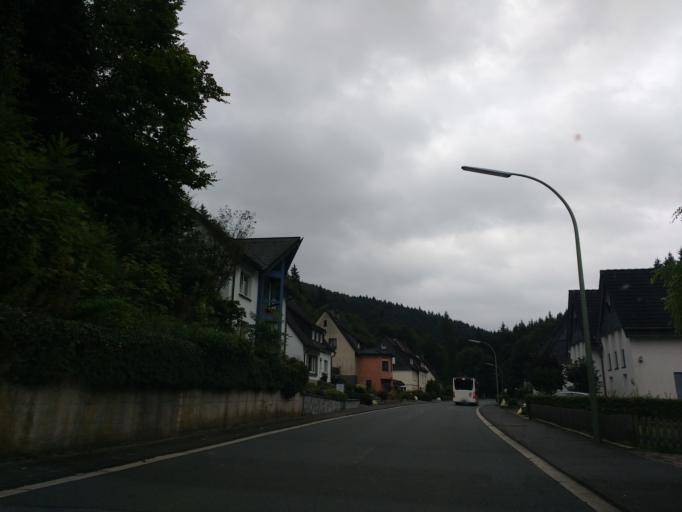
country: DE
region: North Rhine-Westphalia
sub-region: Regierungsbezirk Arnsberg
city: Bestwig
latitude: 51.3583
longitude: 8.4188
